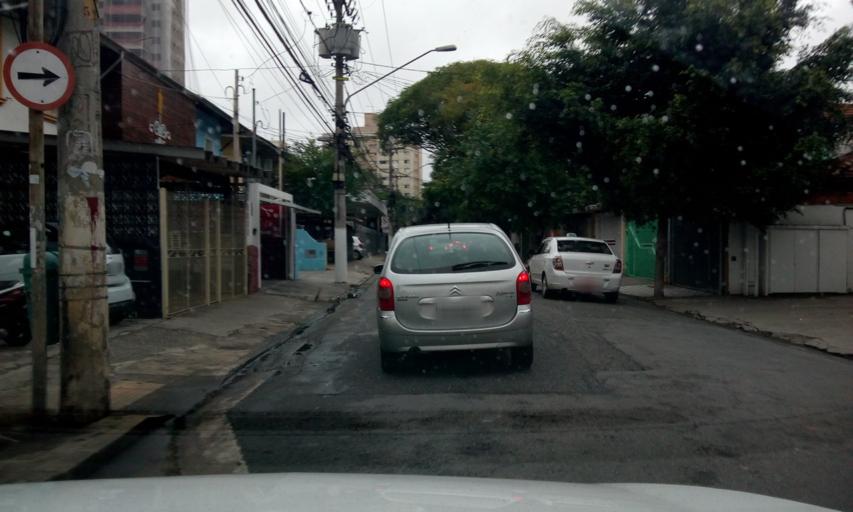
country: BR
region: Sao Paulo
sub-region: Sao Paulo
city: Sao Paulo
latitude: -23.5992
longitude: -46.6806
